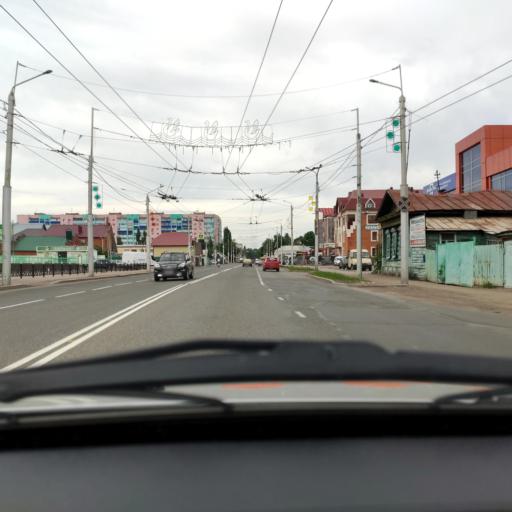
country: RU
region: Bashkortostan
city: Sterlitamak
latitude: 53.6151
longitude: 55.9569
